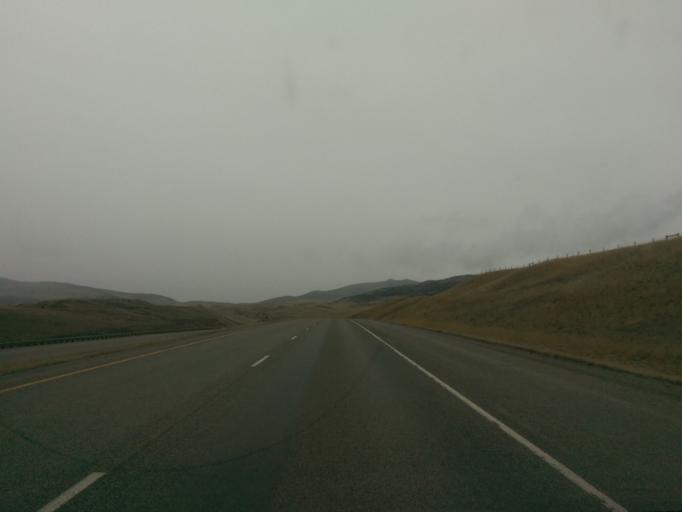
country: US
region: Montana
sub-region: Gallatin County
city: Three Forks
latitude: 45.9100
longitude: -111.7853
